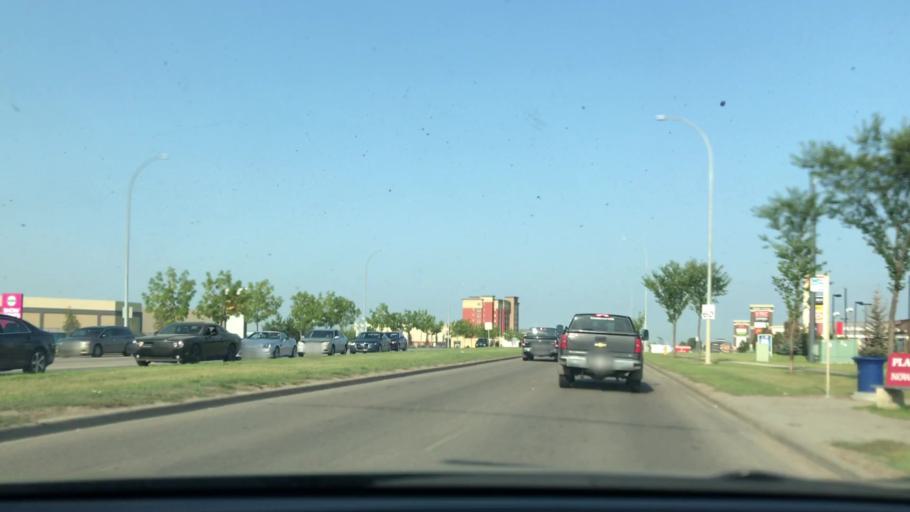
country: CA
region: Alberta
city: Beaumont
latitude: 53.4252
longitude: -113.4803
